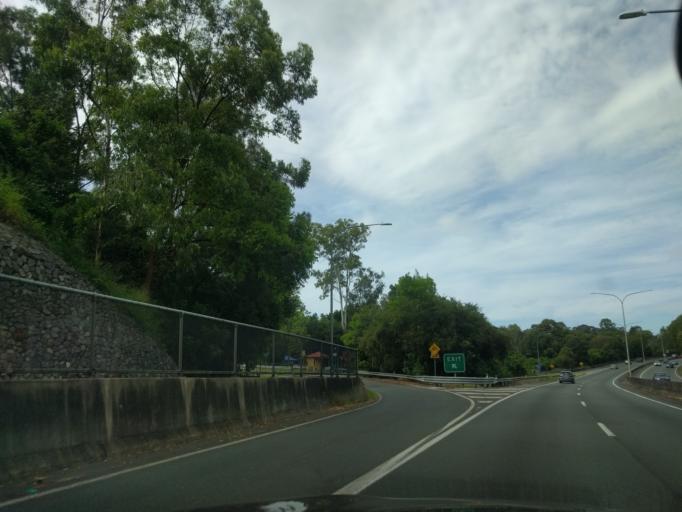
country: AU
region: Queensland
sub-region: Brisbane
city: Kenmore Hills
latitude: -27.5171
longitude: 152.9552
